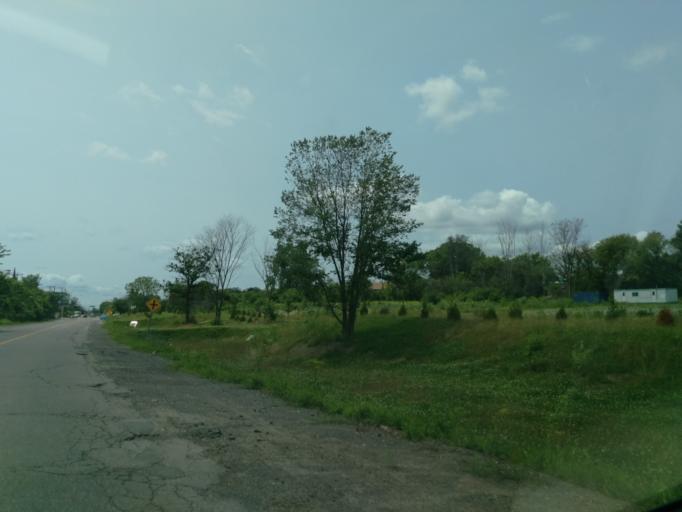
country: CA
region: Ontario
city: Bells Corners
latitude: 45.3875
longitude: -75.8012
